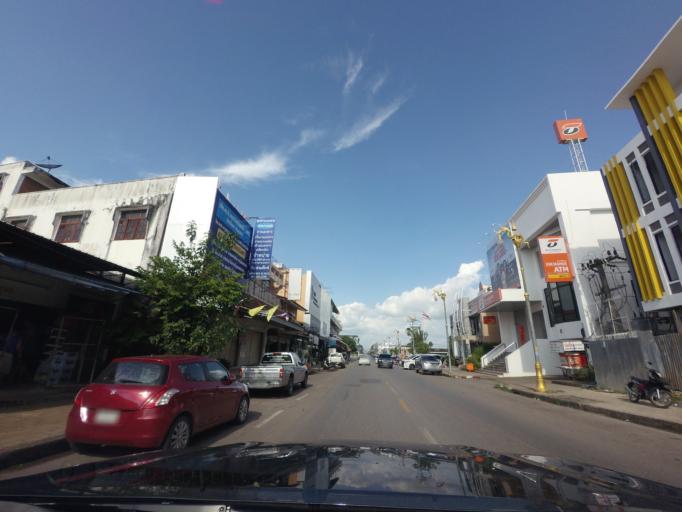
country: TH
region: Nong Khai
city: Nong Khai
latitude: 17.8801
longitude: 102.7437
